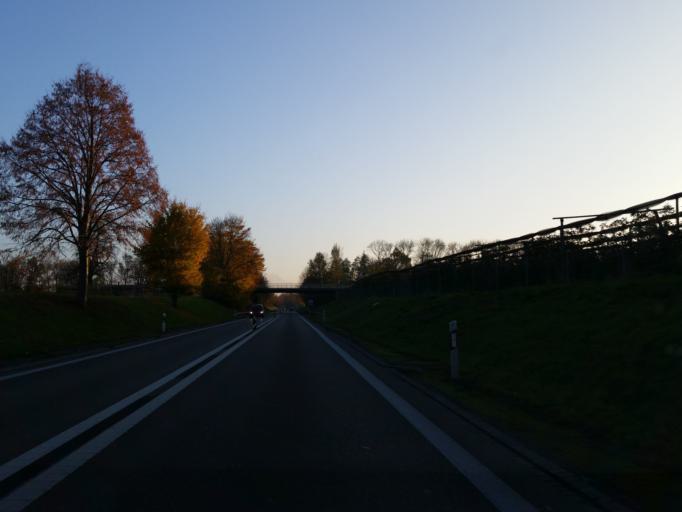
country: CH
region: Thurgau
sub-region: Arbon District
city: Egnach
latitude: 47.5302
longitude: 9.3994
